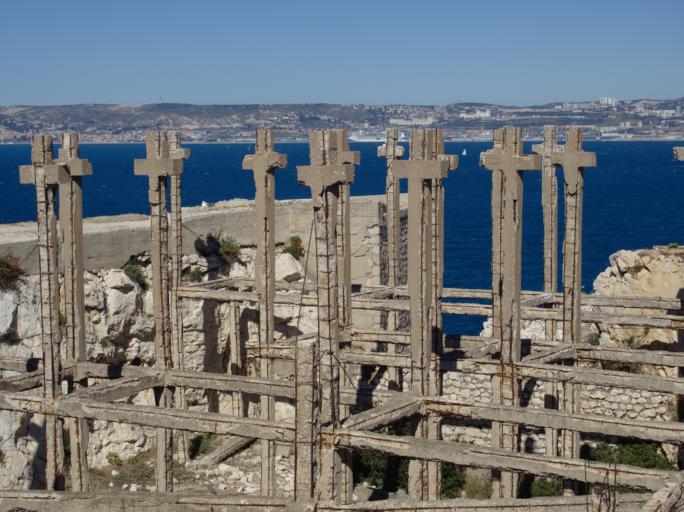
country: FR
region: Provence-Alpes-Cote d'Azur
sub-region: Departement des Bouches-du-Rhone
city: Marseille 07
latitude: 43.2837
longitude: 5.3095
